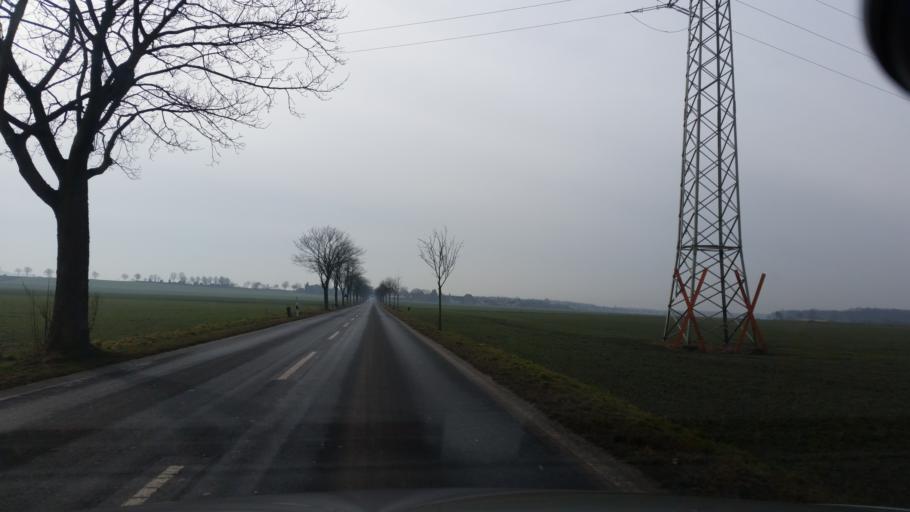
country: DE
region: Lower Saxony
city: Seelze
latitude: 52.3832
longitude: 9.5948
